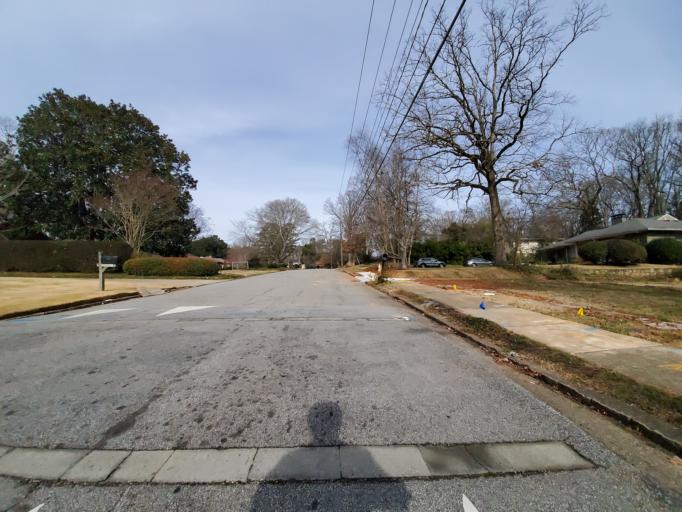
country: US
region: Georgia
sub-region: DeKalb County
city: North Decatur
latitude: 33.7751
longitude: -84.3163
